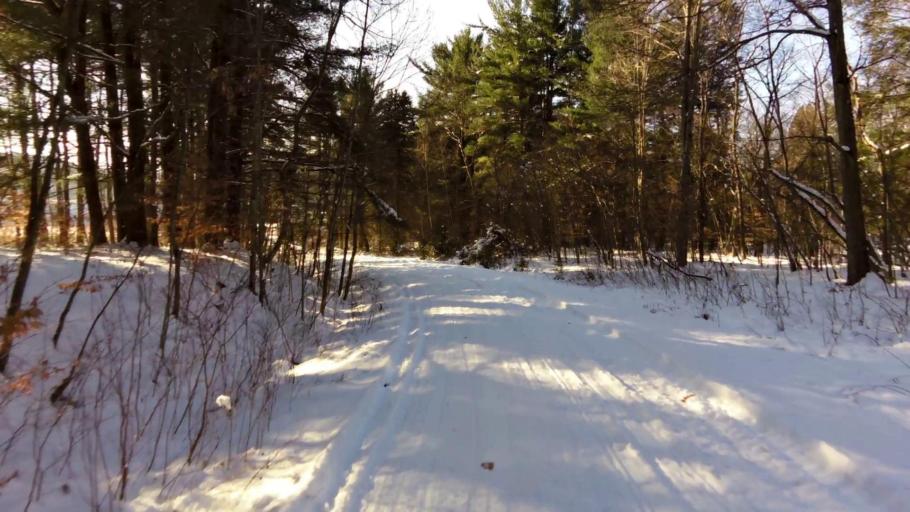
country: US
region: New York
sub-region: Cattaraugus County
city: Salamanca
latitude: 42.1083
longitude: -78.7481
